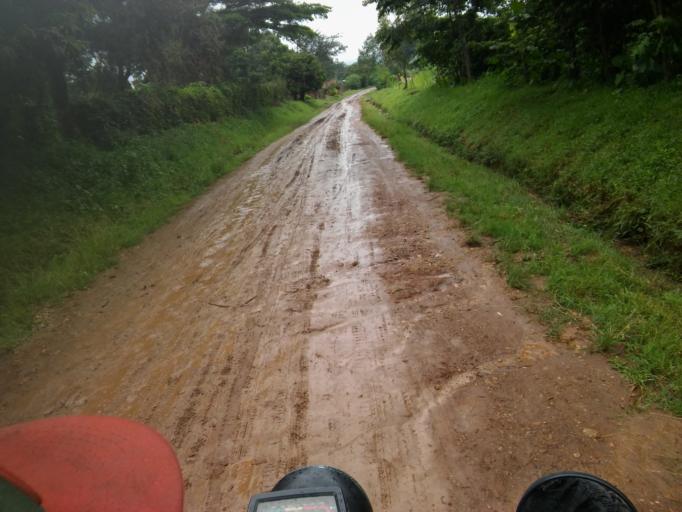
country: UG
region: Eastern Region
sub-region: Mbale District
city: Mbale
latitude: 1.0330
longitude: 34.2010
